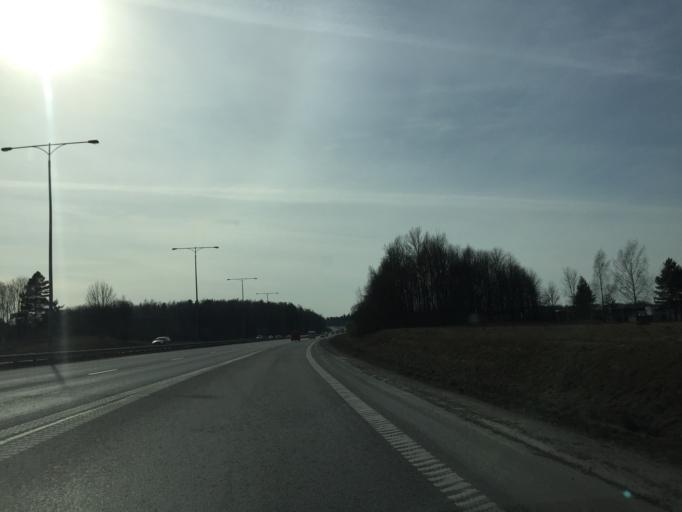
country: SE
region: OErebro
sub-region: Orebro Kommun
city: Orebro
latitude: 59.2572
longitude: 15.1635
